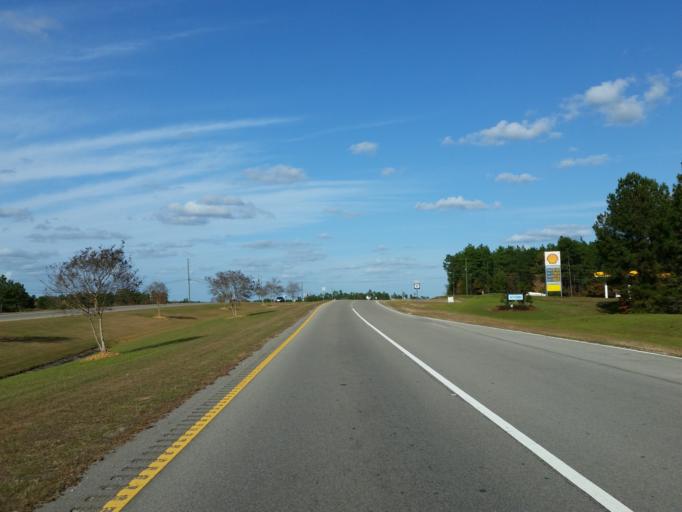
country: US
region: Mississippi
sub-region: Lamar County
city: West Hattiesburg
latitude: 31.2625
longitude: -89.3364
